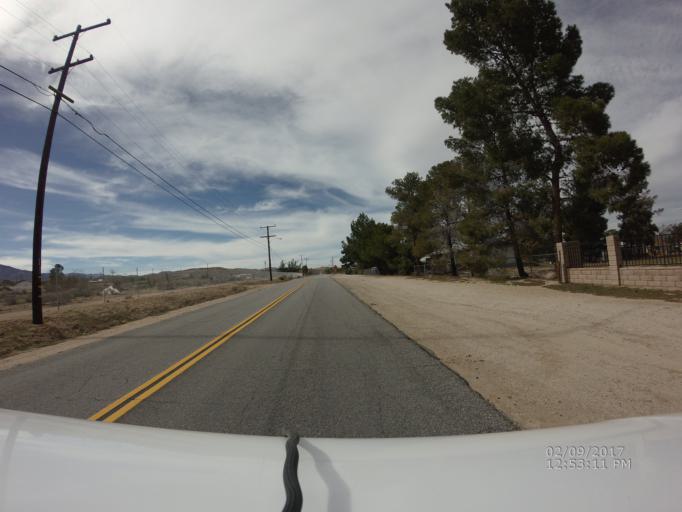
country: US
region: California
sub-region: Los Angeles County
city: Littlerock
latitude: 34.4992
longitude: -117.8947
